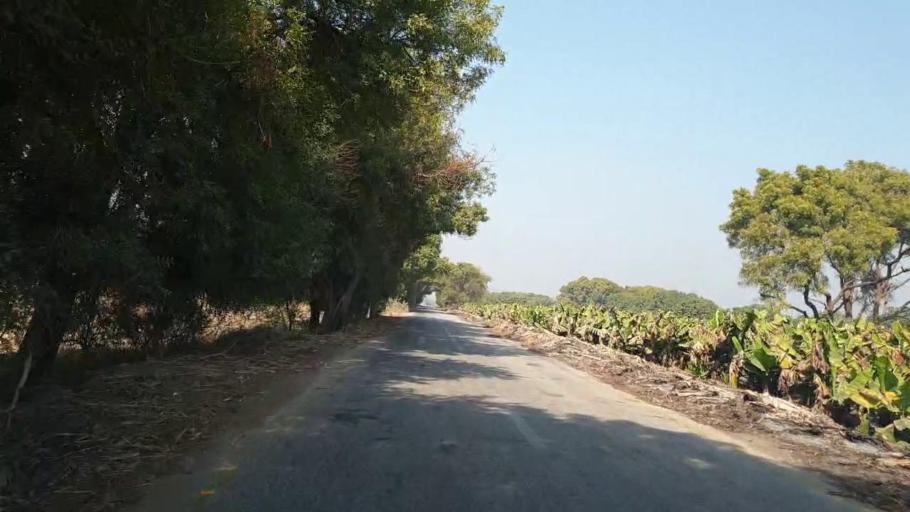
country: PK
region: Sindh
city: Matiari
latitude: 25.5320
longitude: 68.4900
